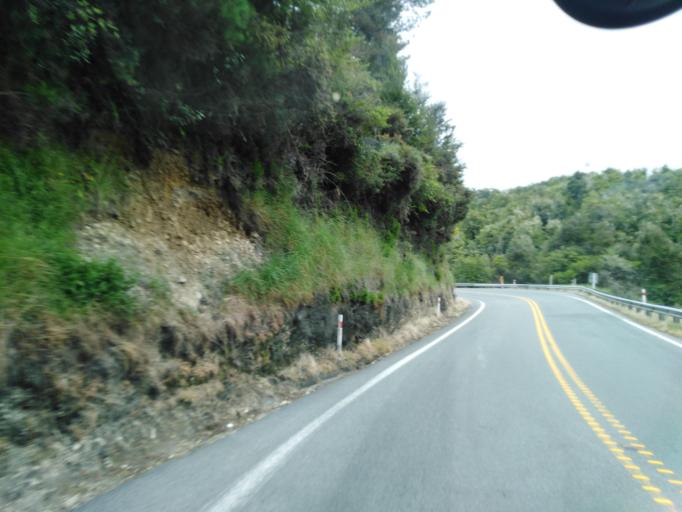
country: NZ
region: Tasman
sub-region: Tasman District
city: Wakefield
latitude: -41.6267
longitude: 172.7281
